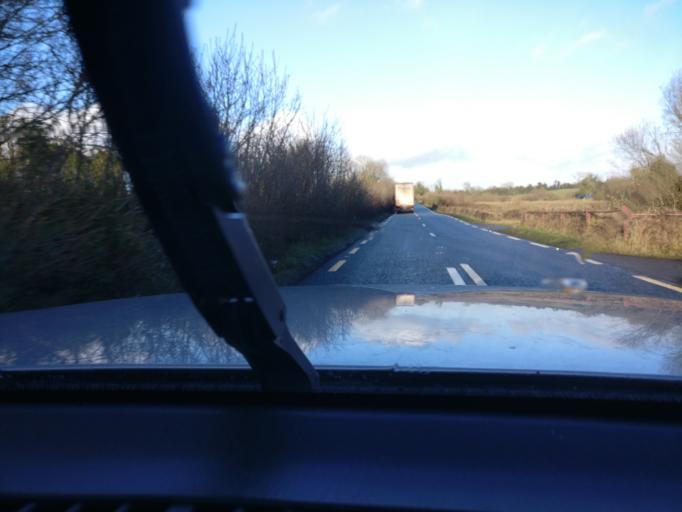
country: IE
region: Leinster
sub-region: An Mhi
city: Athboy
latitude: 53.6521
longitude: -7.0280
